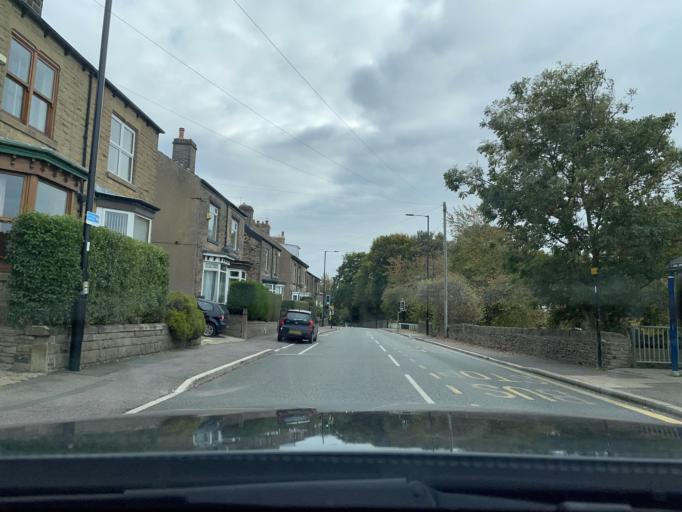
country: GB
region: England
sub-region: Sheffield
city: Sheffield
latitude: 53.3782
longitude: -1.5161
